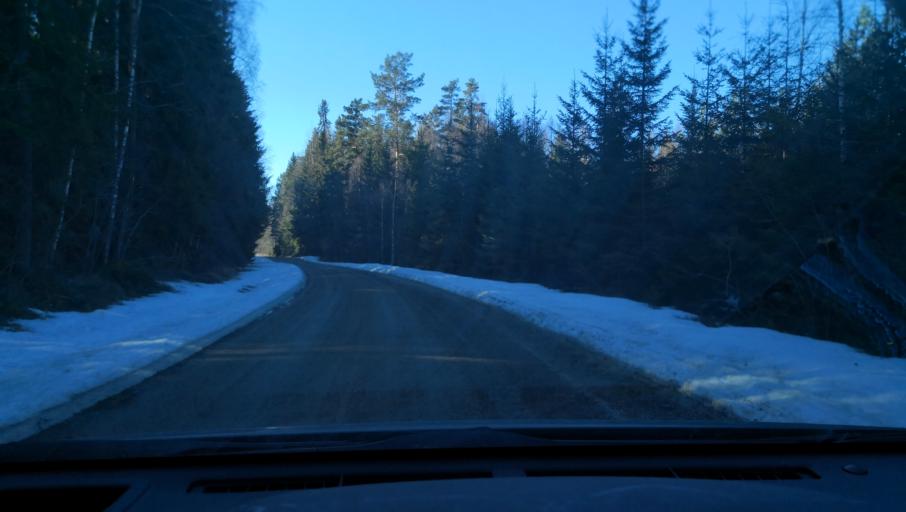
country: SE
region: Vaestmanland
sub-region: Sala Kommun
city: Sala
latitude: 60.1438
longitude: 16.6476
